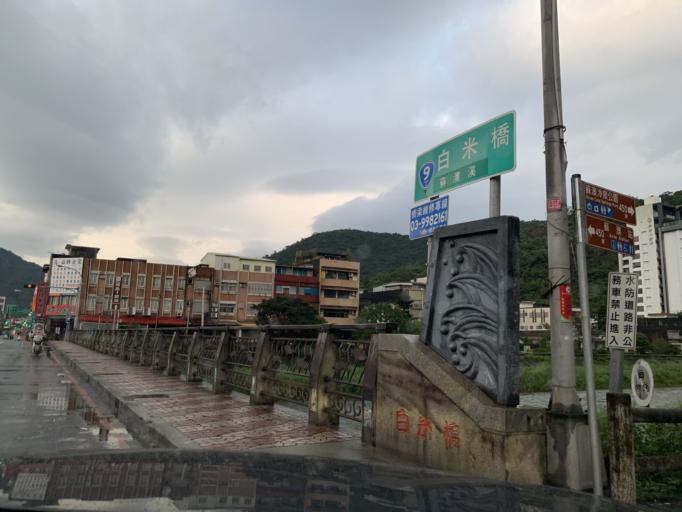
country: TW
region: Taiwan
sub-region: Yilan
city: Yilan
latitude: 24.5960
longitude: 121.8540
